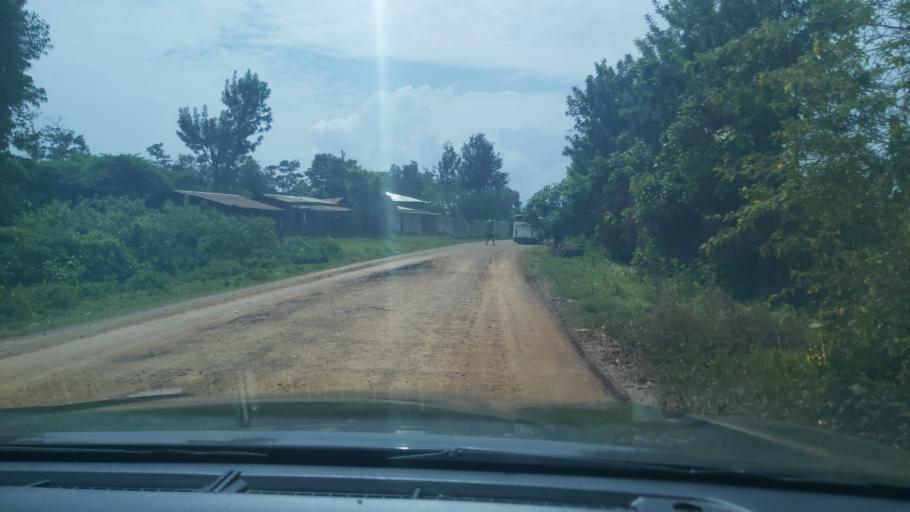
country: ET
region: Oromiya
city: Jima
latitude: 7.7401
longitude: 36.7758
